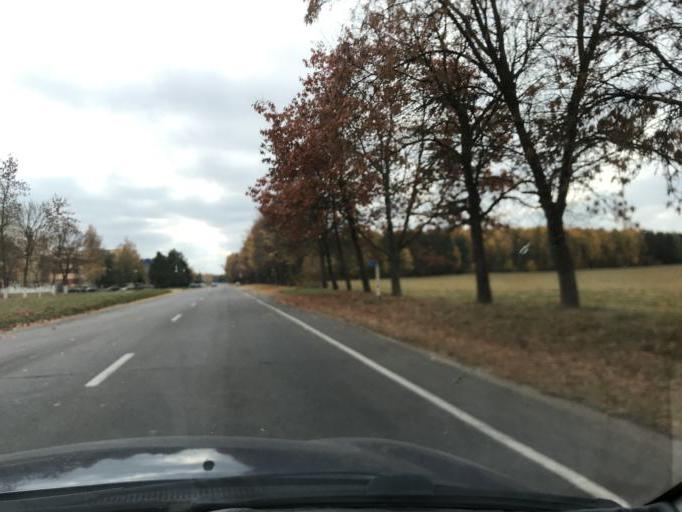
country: BY
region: Grodnenskaya
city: Lida
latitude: 53.9431
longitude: 25.2457
